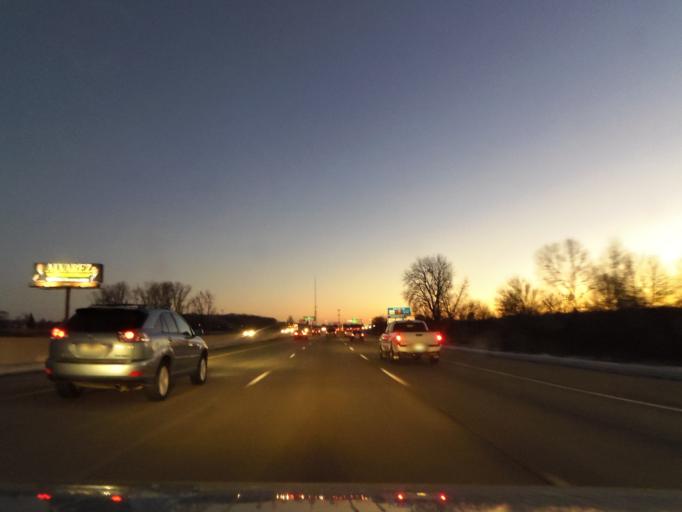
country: US
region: Indiana
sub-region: Lake County
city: Merrillville
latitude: 41.4940
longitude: -87.3199
